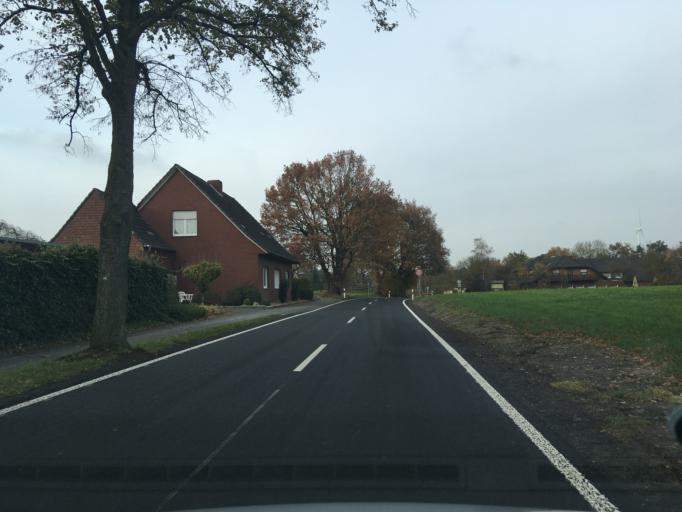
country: DE
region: North Rhine-Westphalia
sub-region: Regierungsbezirk Munster
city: Velen
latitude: 51.9157
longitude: 6.9634
